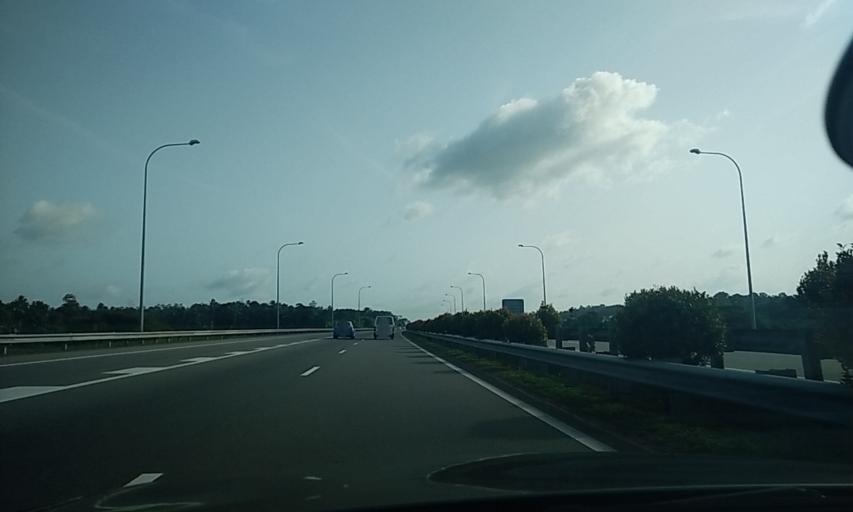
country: LK
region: Western
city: Homagama
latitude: 6.8859
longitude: 79.9766
